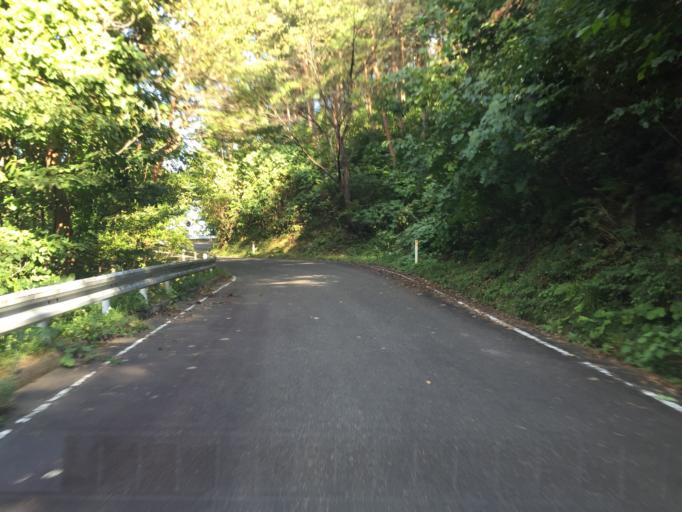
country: JP
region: Fukushima
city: Yanagawamachi-saiwaicho
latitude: 37.8417
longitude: 140.6937
